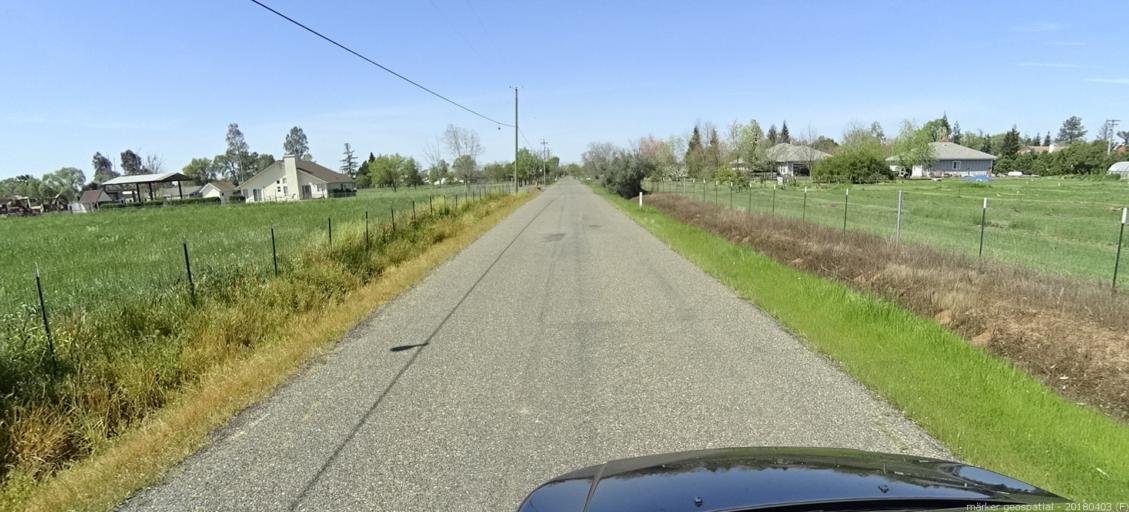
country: US
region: California
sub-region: Sacramento County
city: Wilton
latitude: 38.4021
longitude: -121.2712
